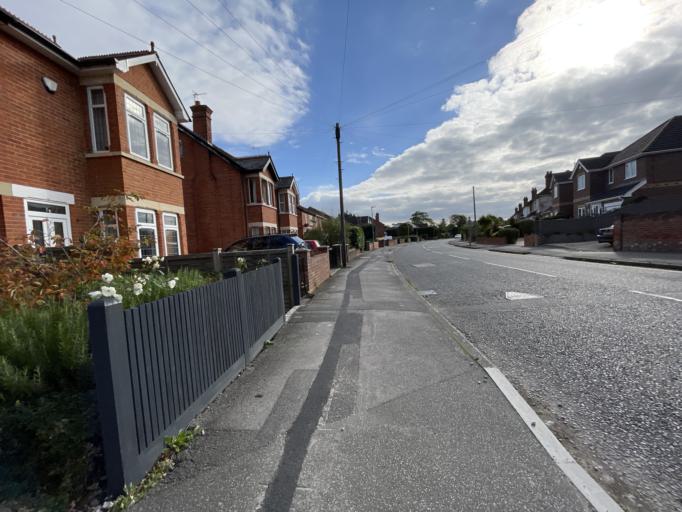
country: GB
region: England
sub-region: West Berkshire
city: Tilehurst
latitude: 51.4560
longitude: -1.0384
